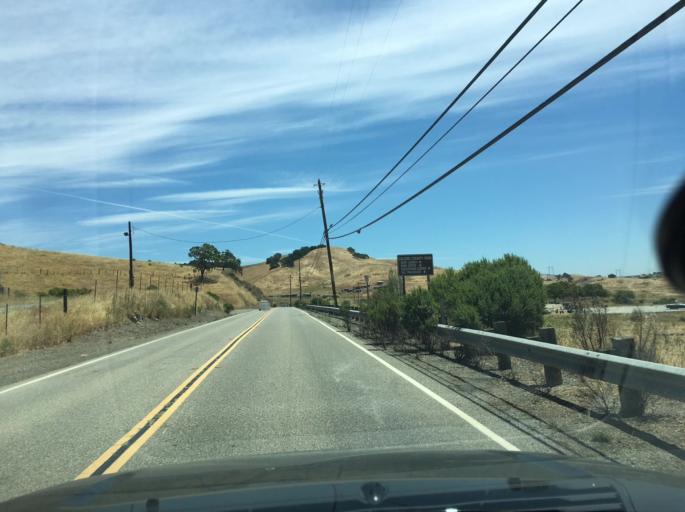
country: US
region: California
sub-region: Santa Clara County
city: Seven Trees
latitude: 37.1883
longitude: -121.7774
